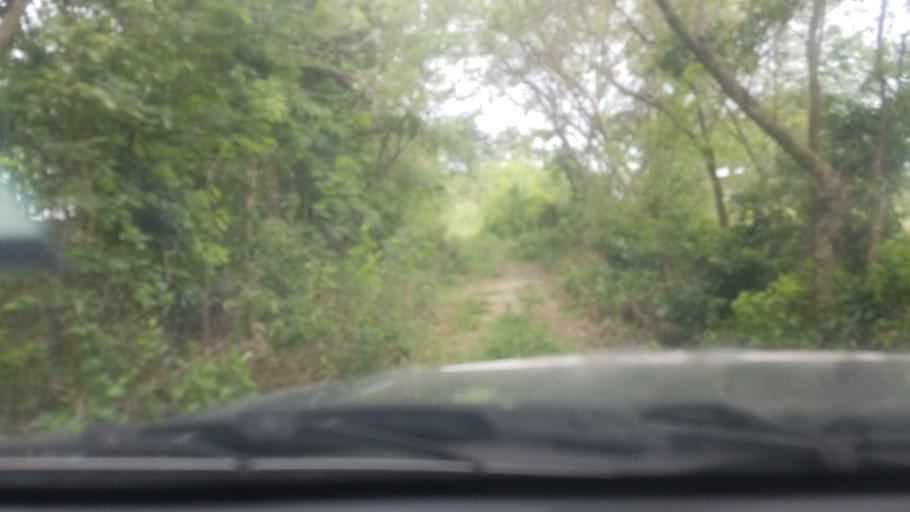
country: LC
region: Laborie Quarter
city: Laborie
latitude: 13.7467
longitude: -60.9784
